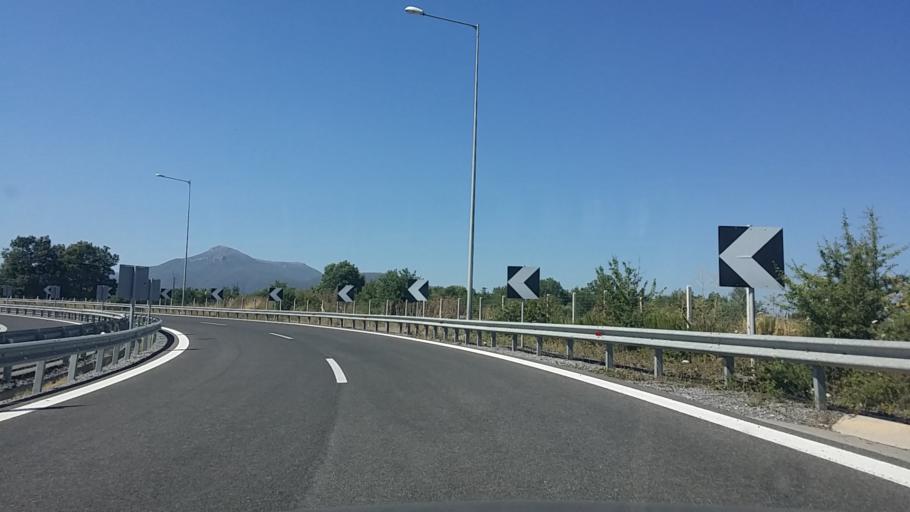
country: GR
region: Peloponnese
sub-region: Nomos Arkadias
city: Megalopoli
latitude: 37.3618
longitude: 22.1469
